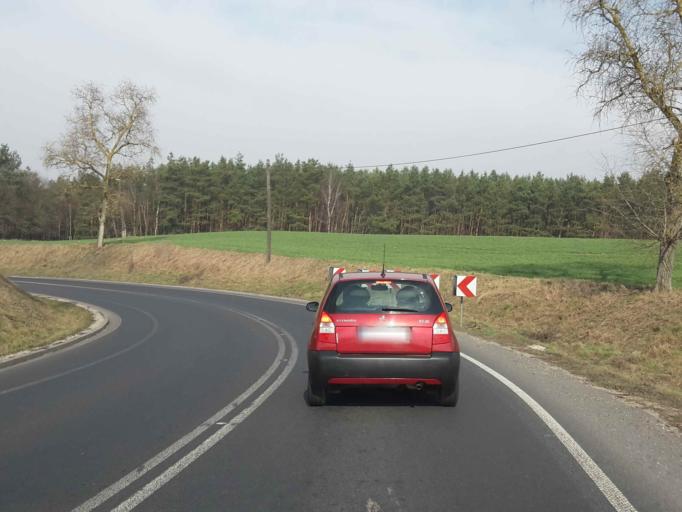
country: PL
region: Kujawsko-Pomorskie
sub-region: Powiat nakielski
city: Naklo nad Notecia
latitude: 53.1074
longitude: 17.6202
